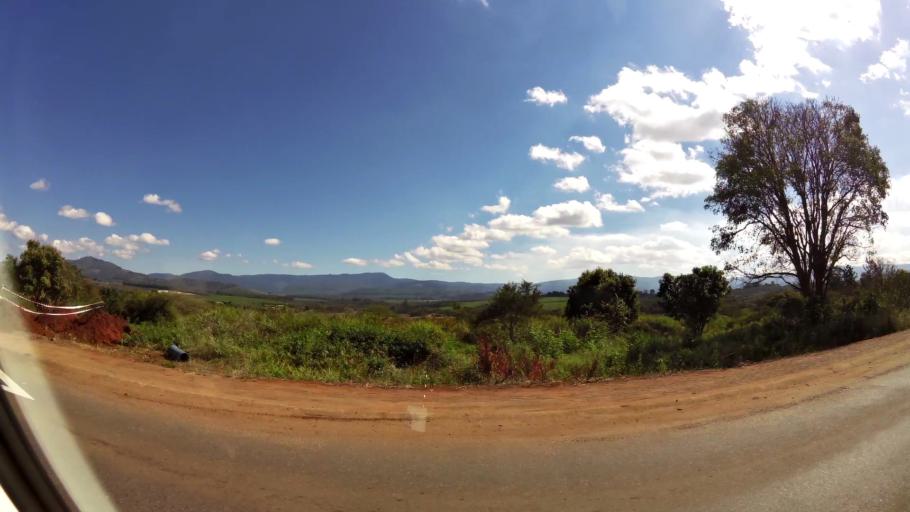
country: ZA
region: Limpopo
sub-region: Mopani District Municipality
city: Tzaneen
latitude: -23.8166
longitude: 30.1458
